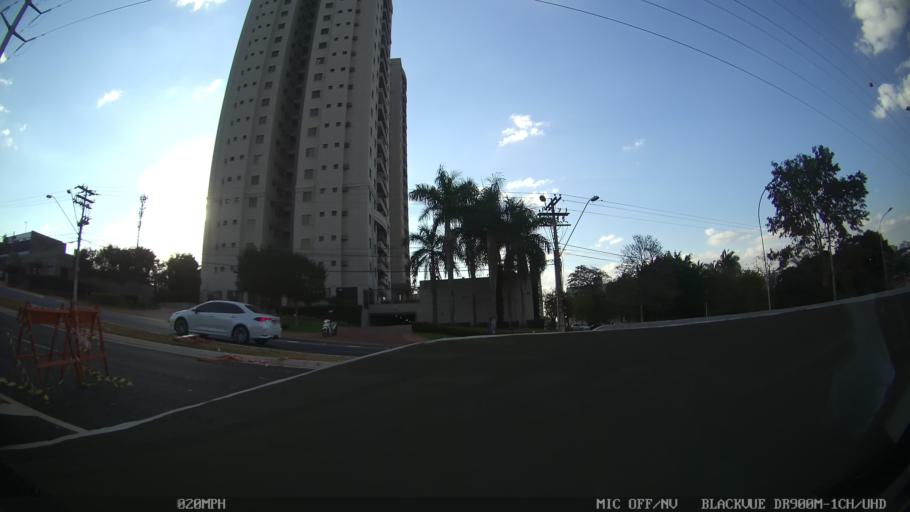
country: BR
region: Sao Paulo
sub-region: Ribeirao Preto
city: Ribeirao Preto
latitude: -21.1930
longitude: -47.7993
